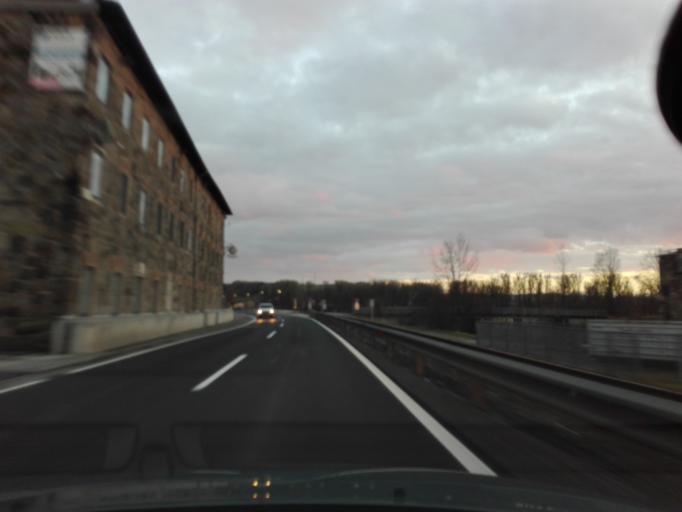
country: AT
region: Upper Austria
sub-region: Politischer Bezirk Perg
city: Bad Kreuzen
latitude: 48.1932
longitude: 14.8182
